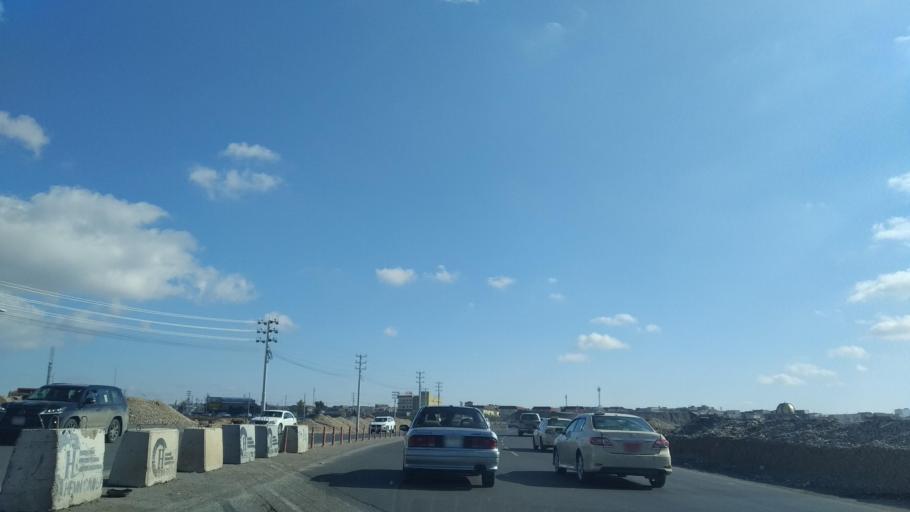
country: IQ
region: Arbil
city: Erbil
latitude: 36.2061
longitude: 44.1265
